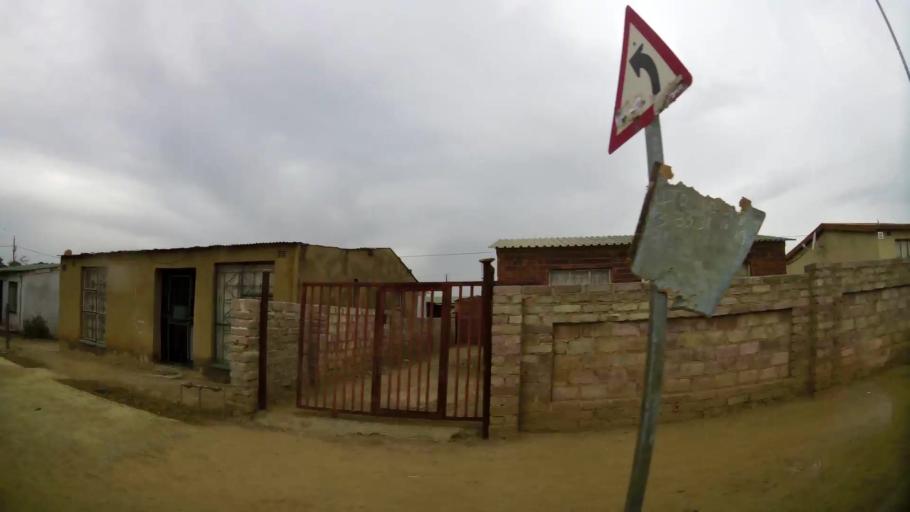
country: ZA
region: Gauteng
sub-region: City of Tshwane Metropolitan Municipality
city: Pretoria
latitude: -25.7099
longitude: 28.3521
